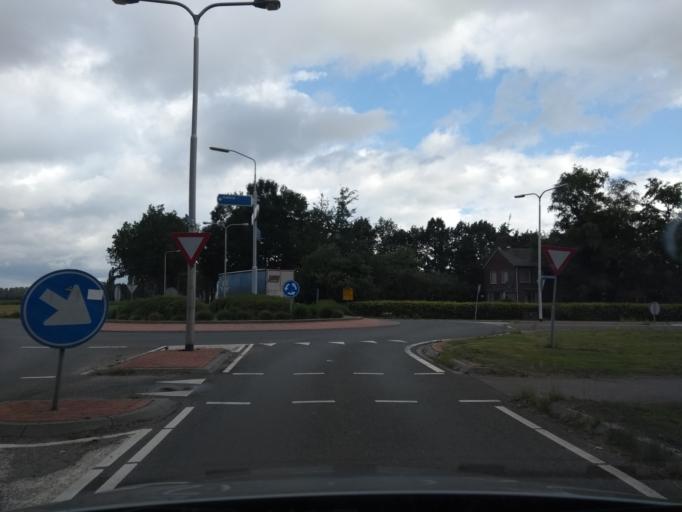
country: NL
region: Overijssel
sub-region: Gemeente Twenterand
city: Vriezenveen
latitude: 52.3828
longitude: 6.6310
